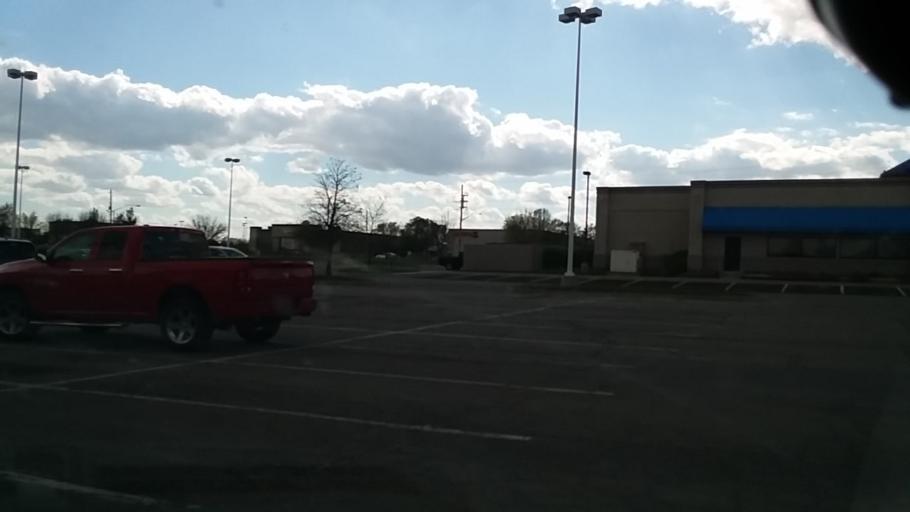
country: US
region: Kansas
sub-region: Douglas County
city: Lawrence
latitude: 38.9277
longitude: -95.2591
